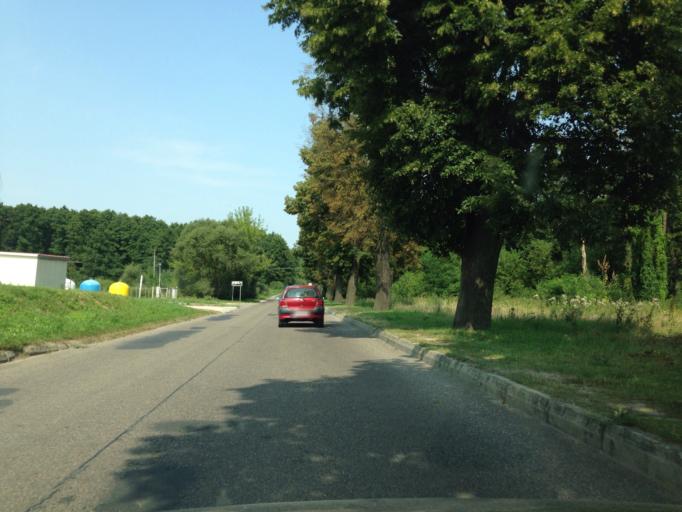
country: PL
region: Kujawsko-Pomorskie
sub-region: Powiat rypinski
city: Rypin
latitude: 53.0762
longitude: 19.4028
